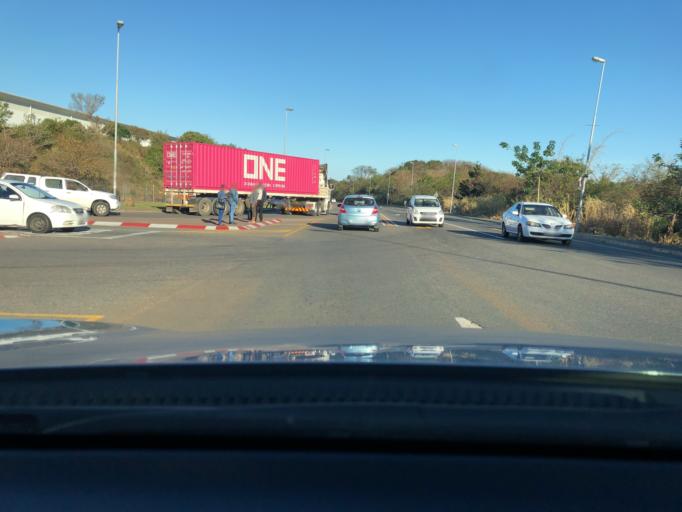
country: ZA
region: KwaZulu-Natal
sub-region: eThekwini Metropolitan Municipality
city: Umkomaas
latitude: -30.0301
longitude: 30.8864
